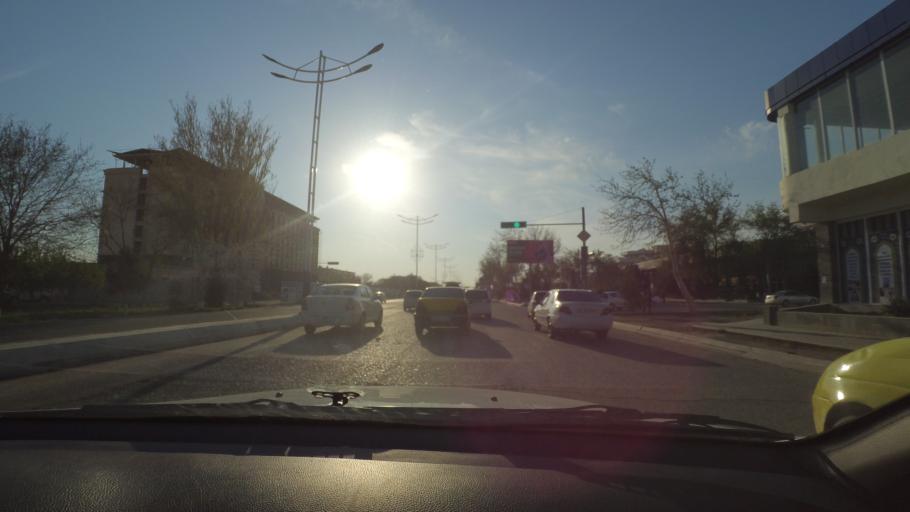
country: UZ
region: Bukhara
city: Bukhara
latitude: 39.7626
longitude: 64.4279
